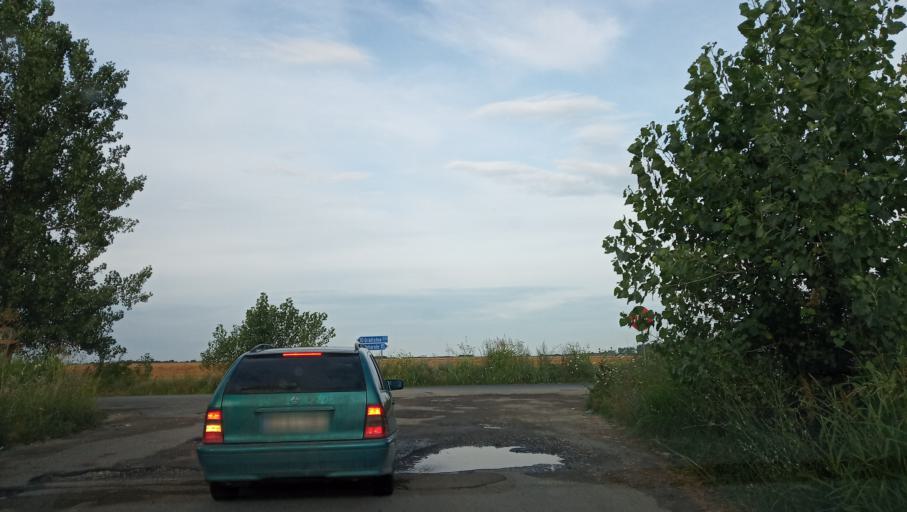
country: RO
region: Giurgiu
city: Gostinari-Vacaresti
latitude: 44.1755
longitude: 26.2086
